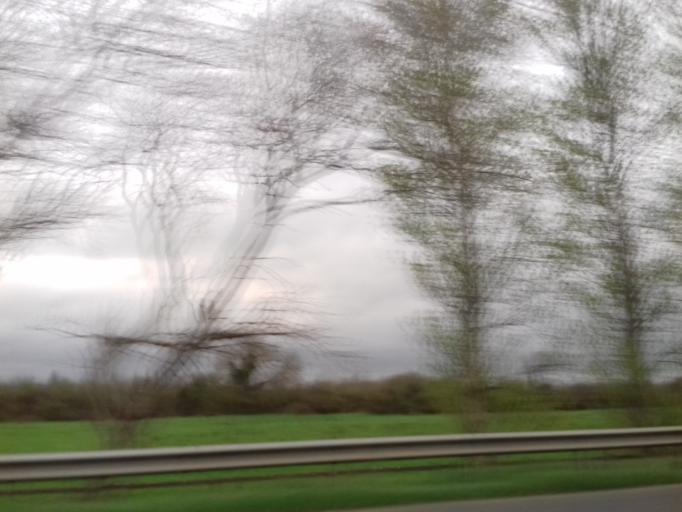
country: IE
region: Munster
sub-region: County Limerick
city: Newcastle West
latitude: 52.4897
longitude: -9.0028
